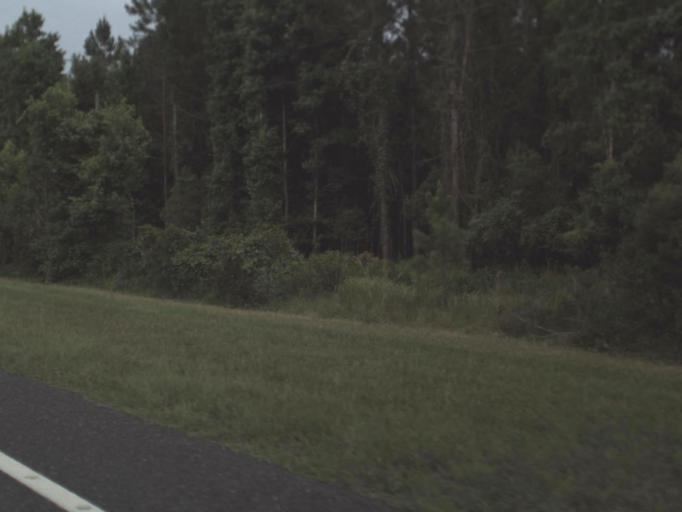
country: US
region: Florida
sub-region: Levy County
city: Inglis
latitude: 29.1731
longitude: -82.6562
